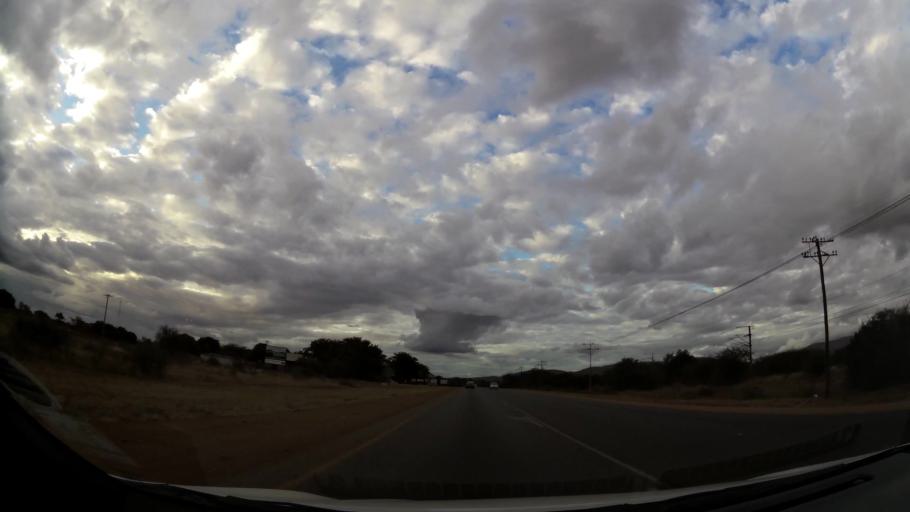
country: ZA
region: Limpopo
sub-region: Waterberg District Municipality
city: Mokopane
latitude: -24.2210
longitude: 29.0039
